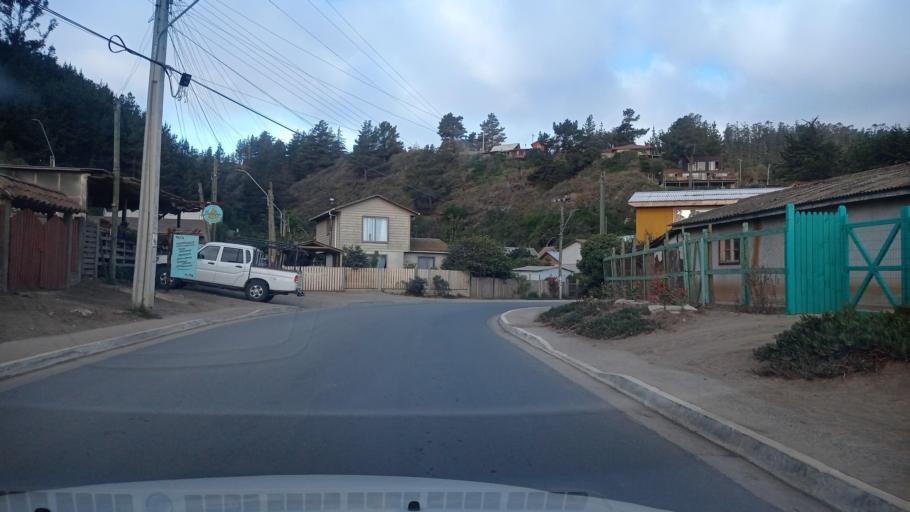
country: CL
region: O'Higgins
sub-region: Provincia de Colchagua
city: Santa Cruz
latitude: -34.4797
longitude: -72.0124
